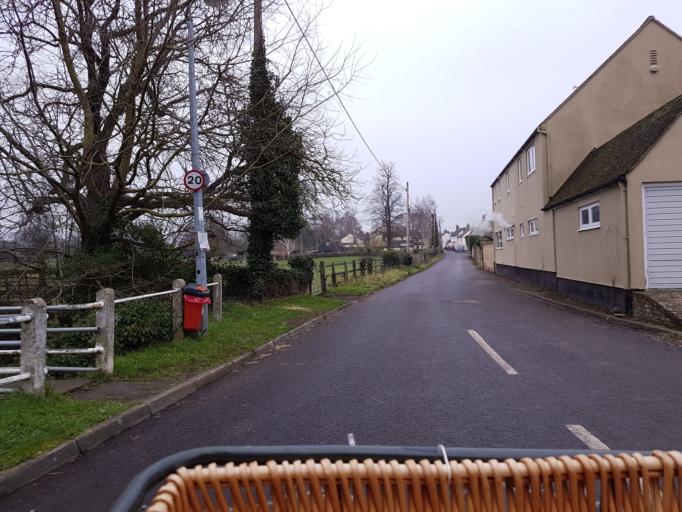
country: GB
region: England
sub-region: Cambridgeshire
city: Duxford
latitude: 52.0663
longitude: 0.1941
